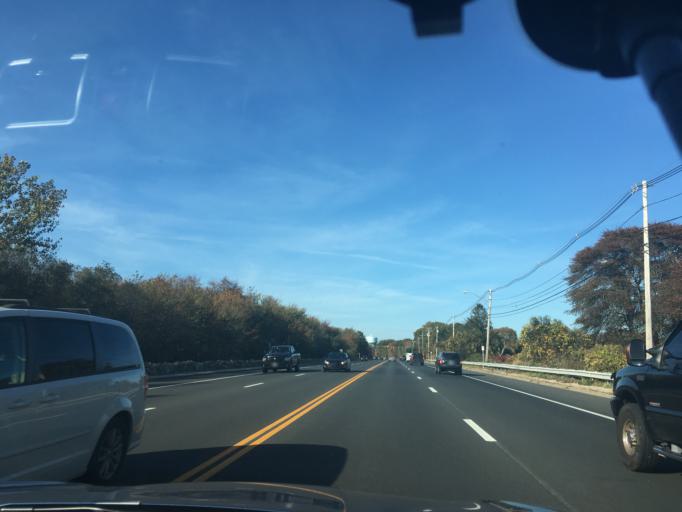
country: US
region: Rhode Island
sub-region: Washington County
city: Narragansett Pier
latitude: 41.4098
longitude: -71.4782
